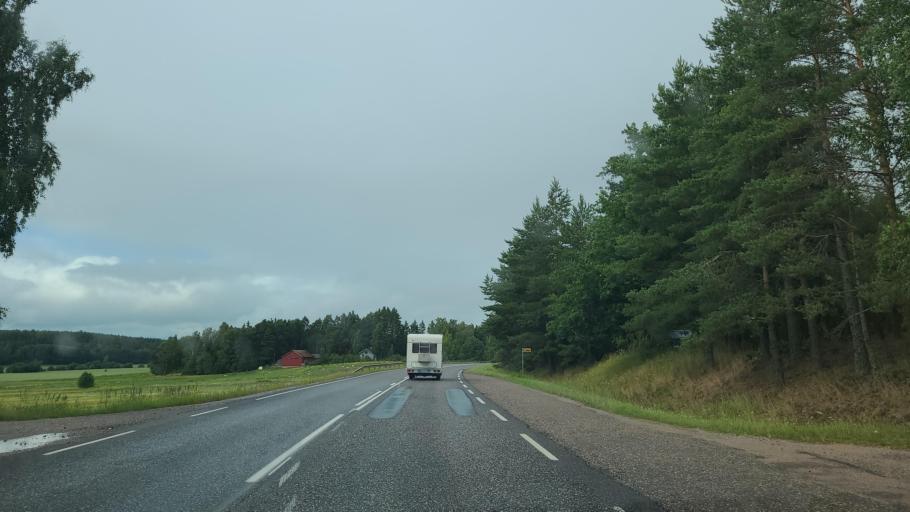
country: FI
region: Varsinais-Suomi
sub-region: Turku
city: Sauvo
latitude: 60.3088
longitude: 22.6871
